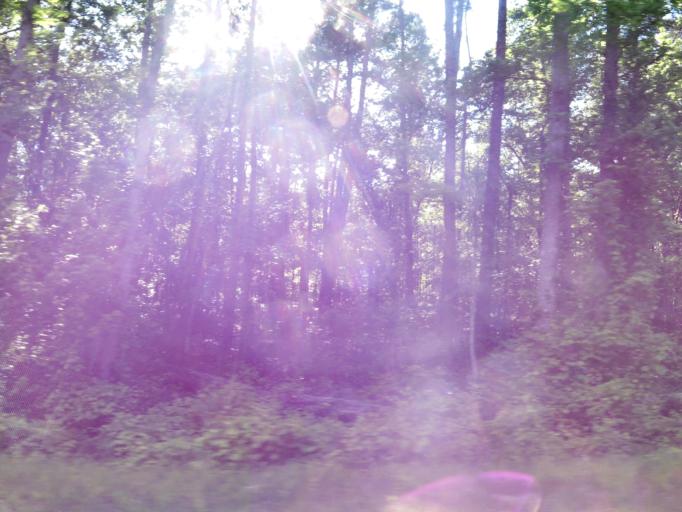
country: US
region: South Carolina
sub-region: Allendale County
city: Fairfax
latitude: 32.9459
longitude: -81.2365
